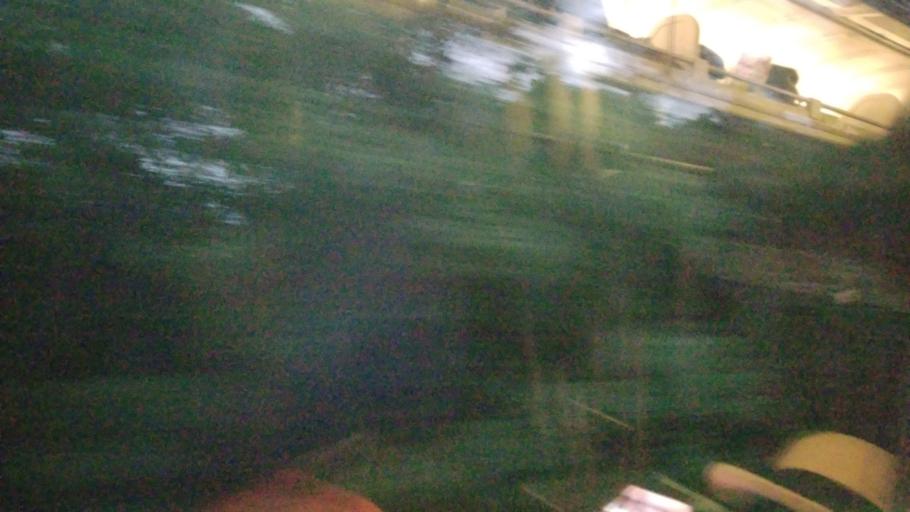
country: US
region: Virginia
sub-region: Orange County
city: Gordonsville
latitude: 38.2047
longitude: -78.2218
